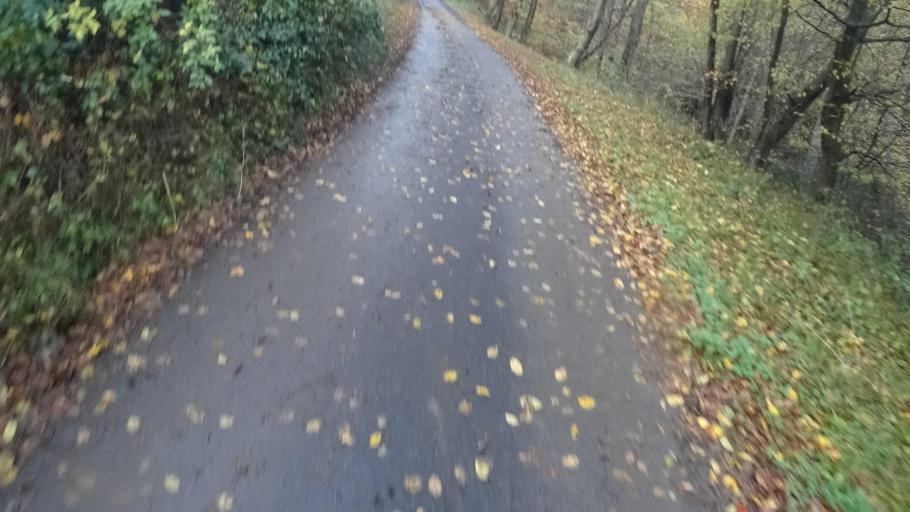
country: DE
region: Rheinland-Pfalz
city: Gondershausen
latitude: 50.1392
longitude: 7.4987
